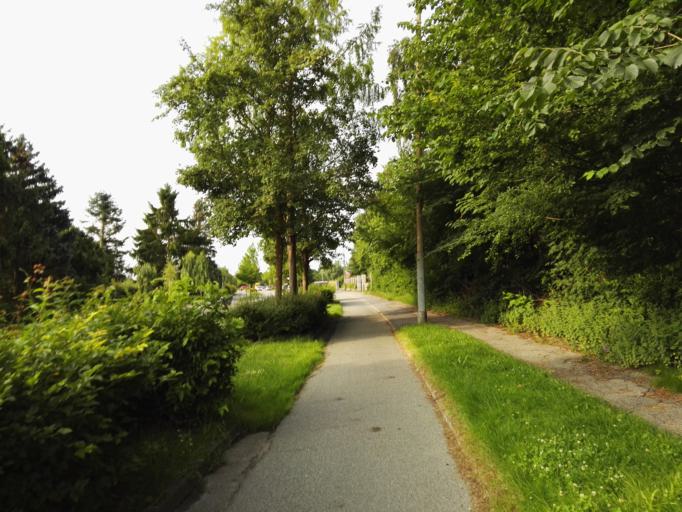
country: DK
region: Capital Region
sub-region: Ballerup Kommune
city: Ballerup
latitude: 55.7457
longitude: 12.3676
